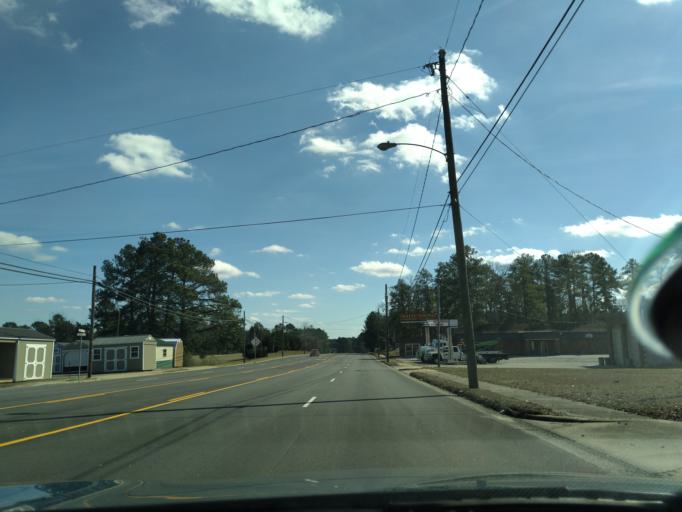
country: US
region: Virginia
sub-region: Nottoway County
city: Crewe
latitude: 37.1671
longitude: -78.1167
